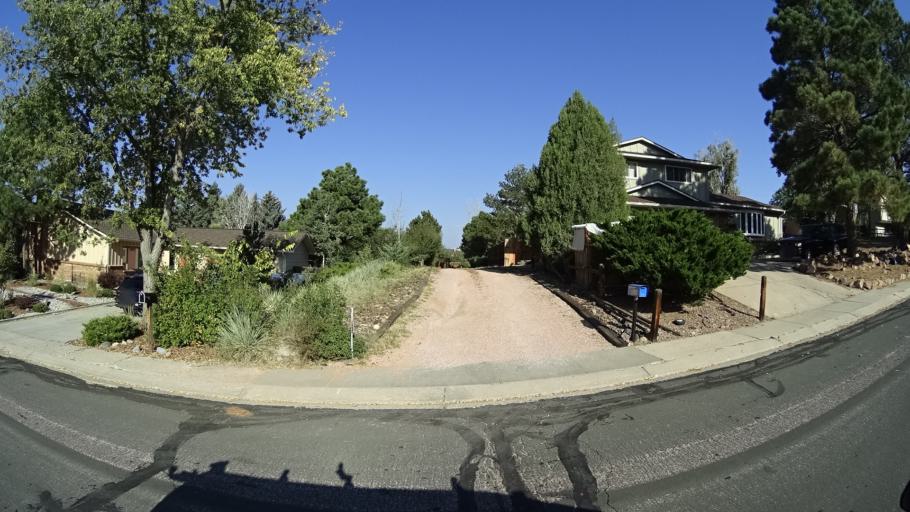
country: US
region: Colorado
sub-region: El Paso County
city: Cimarron Hills
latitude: 38.8929
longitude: -104.7311
